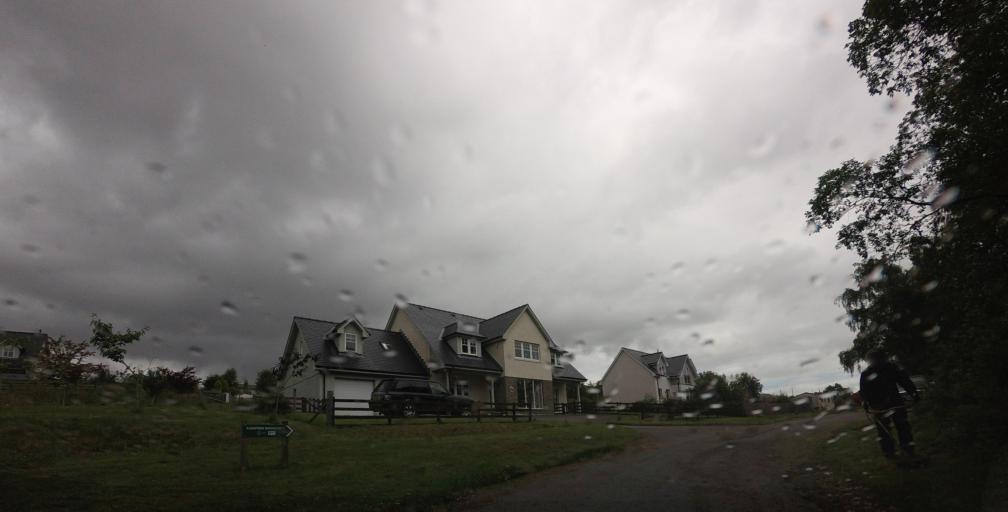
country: GB
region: Scotland
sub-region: Highland
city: Fort William
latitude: 56.8549
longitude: -5.2551
